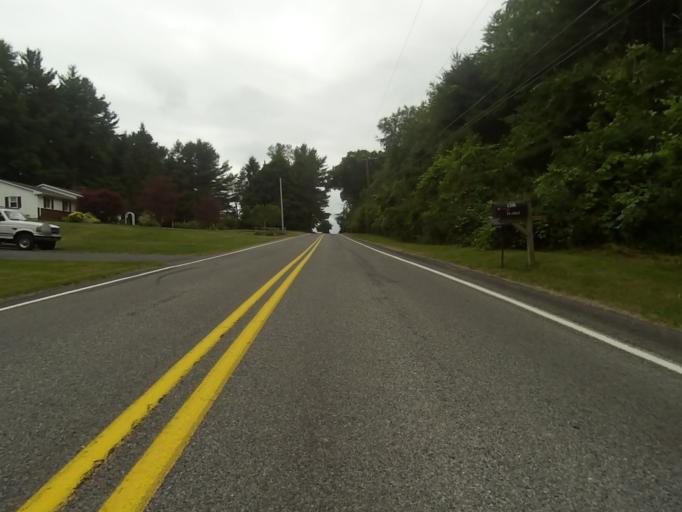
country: US
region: Pennsylvania
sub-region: Centre County
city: Stormstown
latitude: 40.7160
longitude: -78.0027
